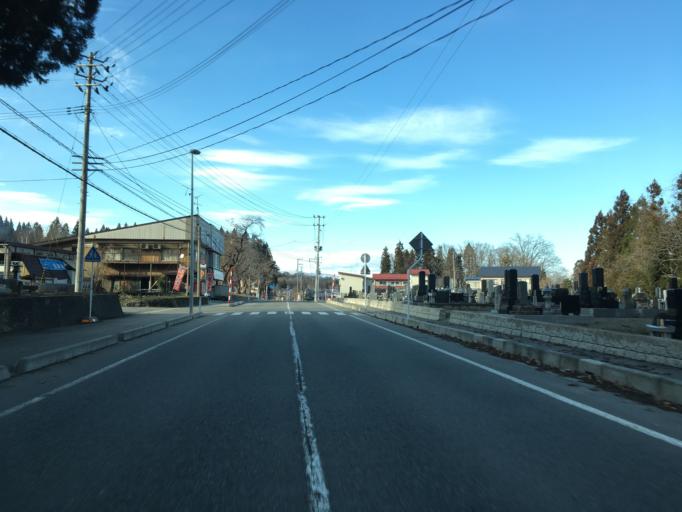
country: JP
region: Yamagata
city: Nagai
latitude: 38.0047
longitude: 139.9602
